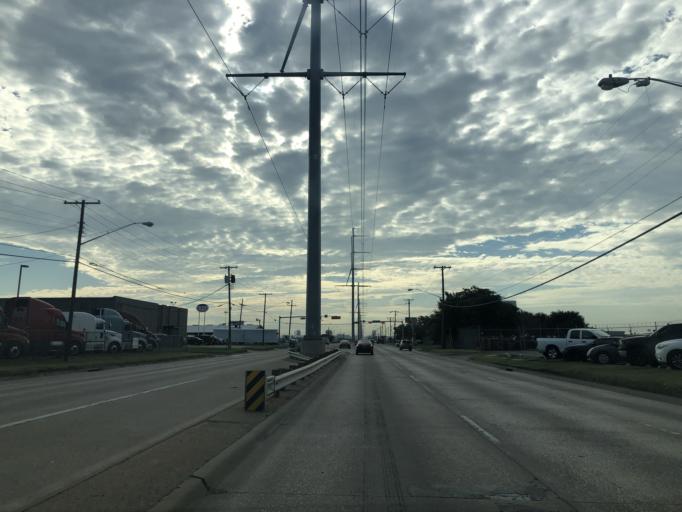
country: US
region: Texas
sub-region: Dallas County
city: Irving
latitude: 32.8081
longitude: -96.8911
